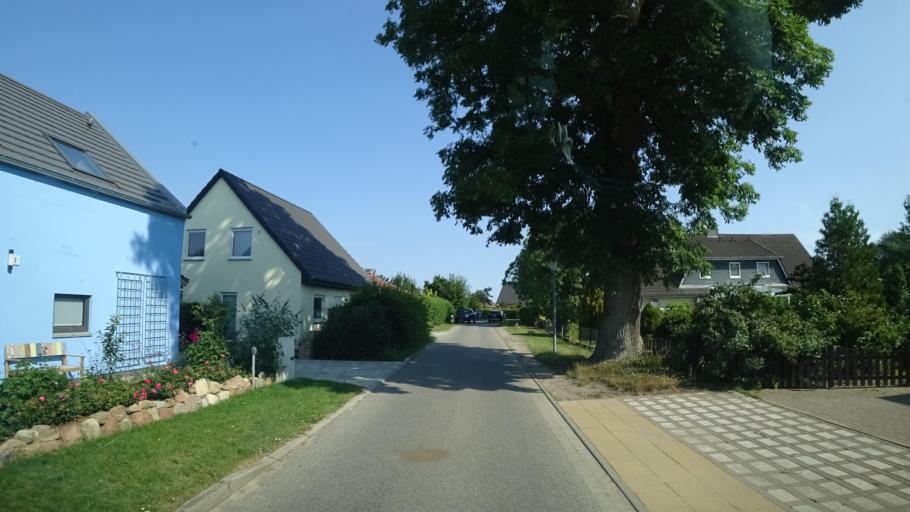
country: DE
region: Mecklenburg-Vorpommern
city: Kemnitz
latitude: 54.1129
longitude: 13.5319
